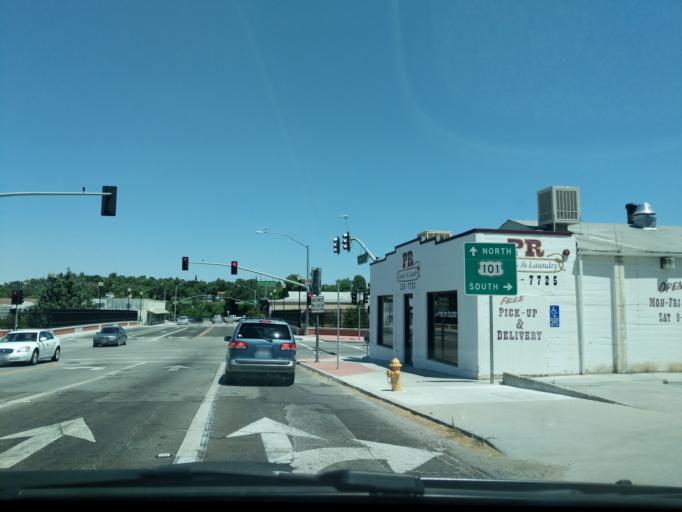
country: US
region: California
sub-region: San Luis Obispo County
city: Paso Robles
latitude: 35.6279
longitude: -120.6874
